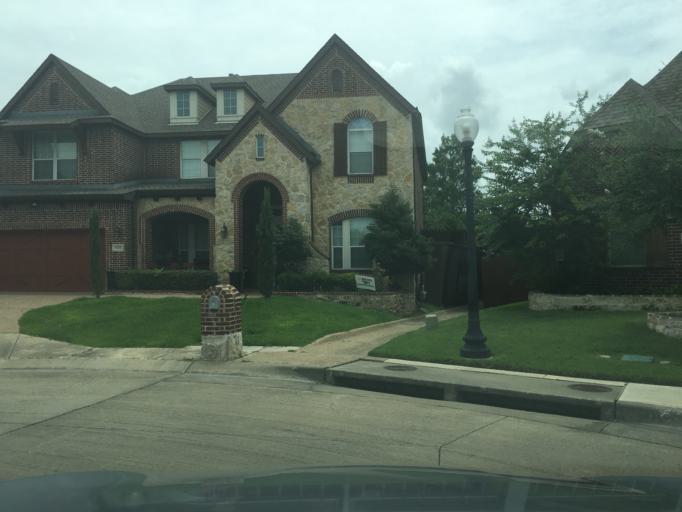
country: US
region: Texas
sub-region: Dallas County
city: Richardson
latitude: 32.9355
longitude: -96.7261
